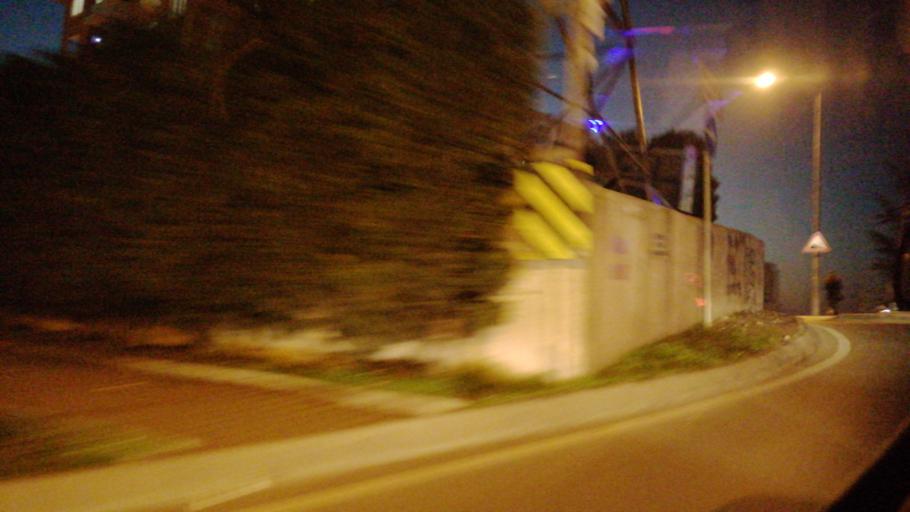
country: TR
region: Istanbul
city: Umraniye
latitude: 41.0050
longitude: 29.1349
